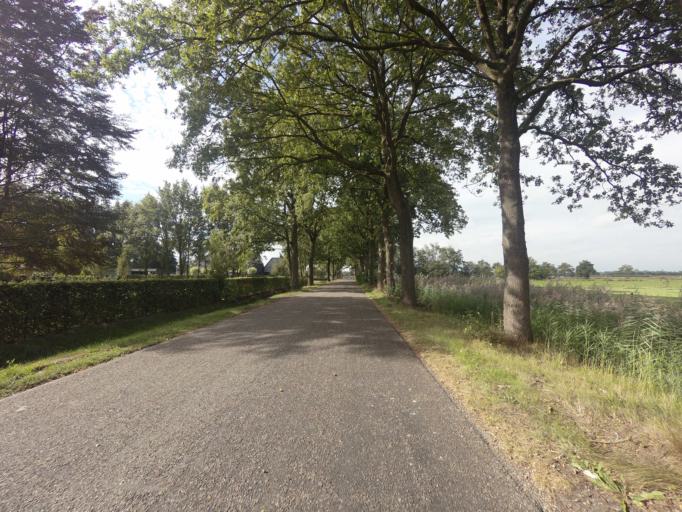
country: NL
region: Friesland
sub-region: Gemeente Opsterland
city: Gorredijk
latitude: 52.9905
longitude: 6.0906
